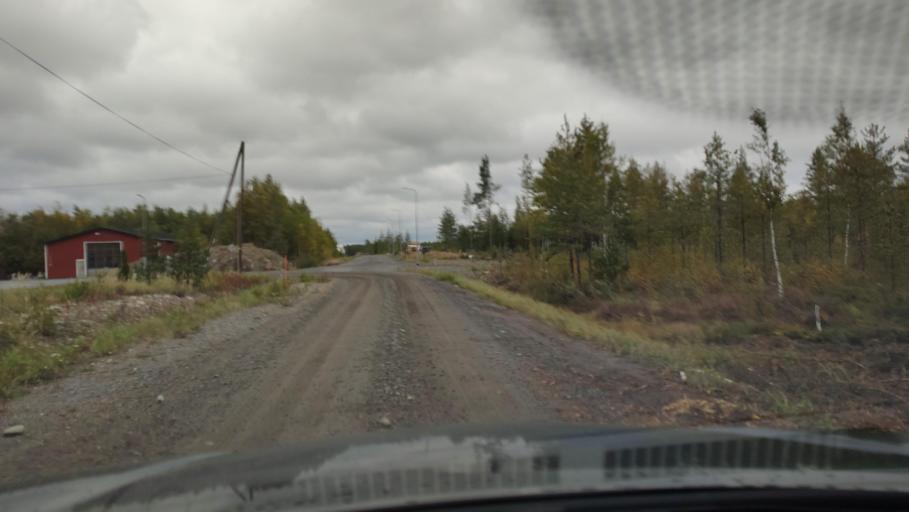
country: FI
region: Ostrobothnia
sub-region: Sydosterbotten
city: Kristinestad
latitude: 62.2272
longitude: 21.5249
